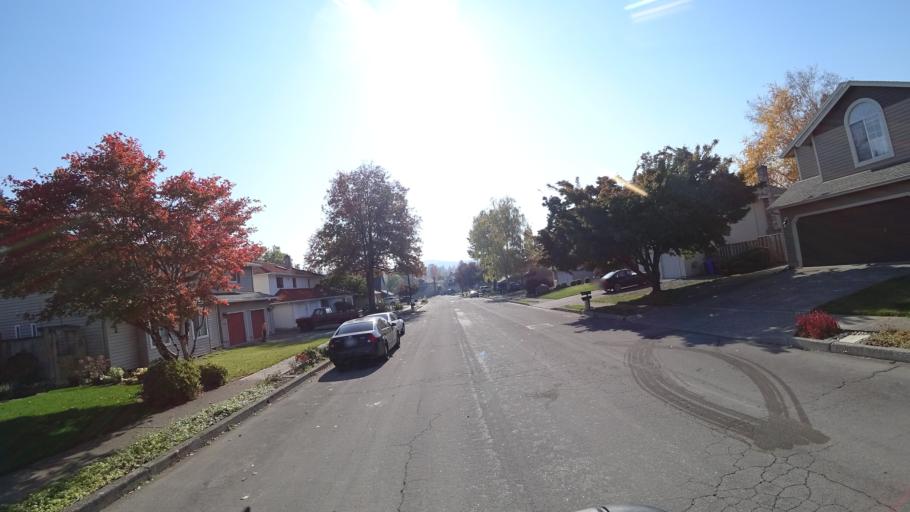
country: US
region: Oregon
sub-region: Multnomah County
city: Gresham
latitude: 45.4928
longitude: -122.4558
